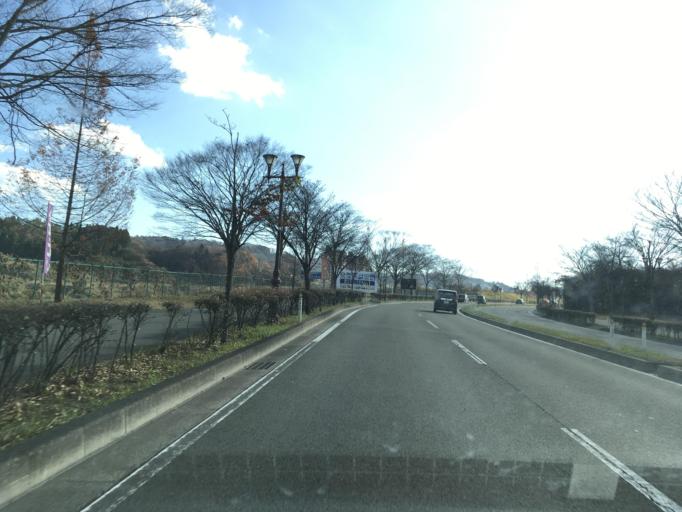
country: JP
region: Miyagi
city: Sendai
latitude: 38.2630
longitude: 140.7626
